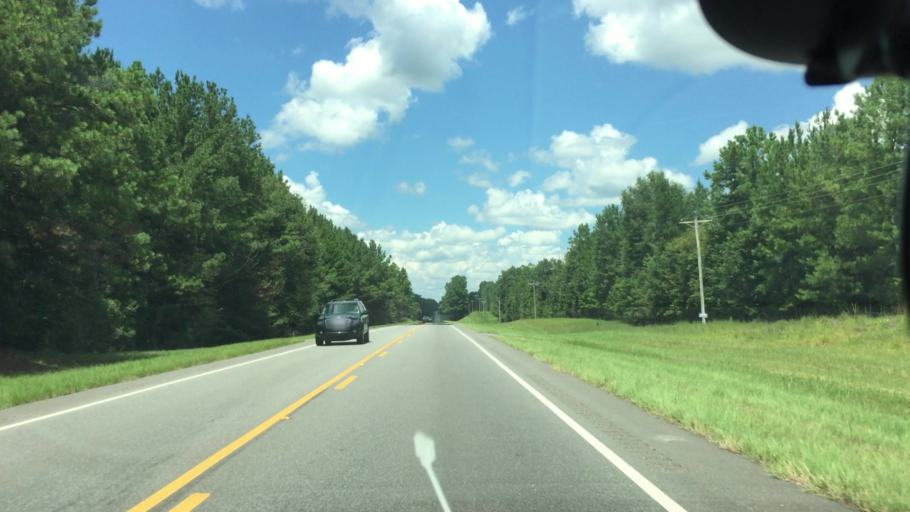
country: US
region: Alabama
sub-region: Coffee County
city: New Brockton
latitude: 31.4990
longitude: -85.9150
